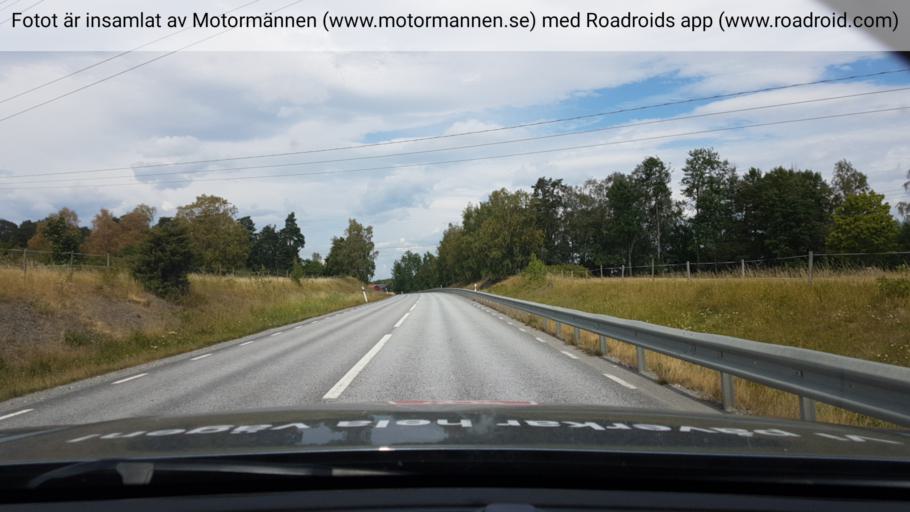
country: SE
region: Uppsala
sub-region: Habo Kommun
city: Balsta
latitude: 59.6159
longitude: 17.6062
